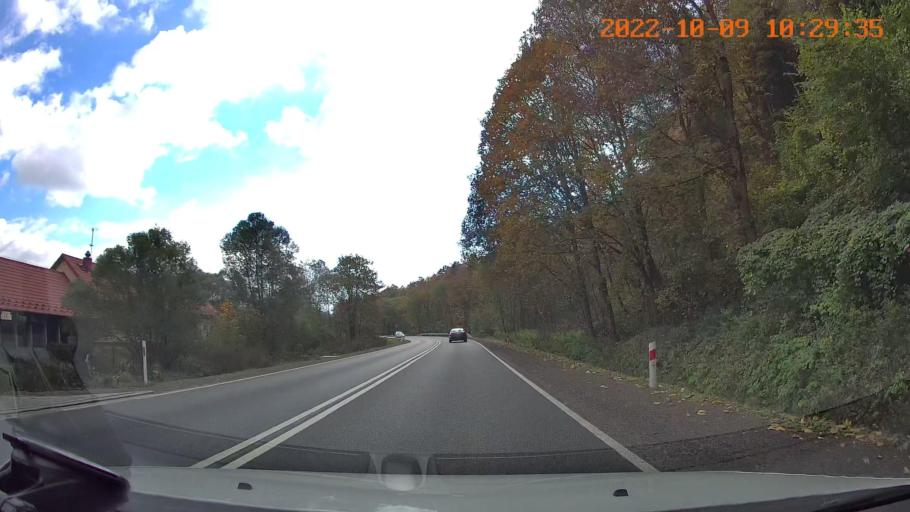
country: PL
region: Lesser Poland Voivodeship
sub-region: Powiat myslenicki
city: Lubien
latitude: 49.7116
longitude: 20.0032
